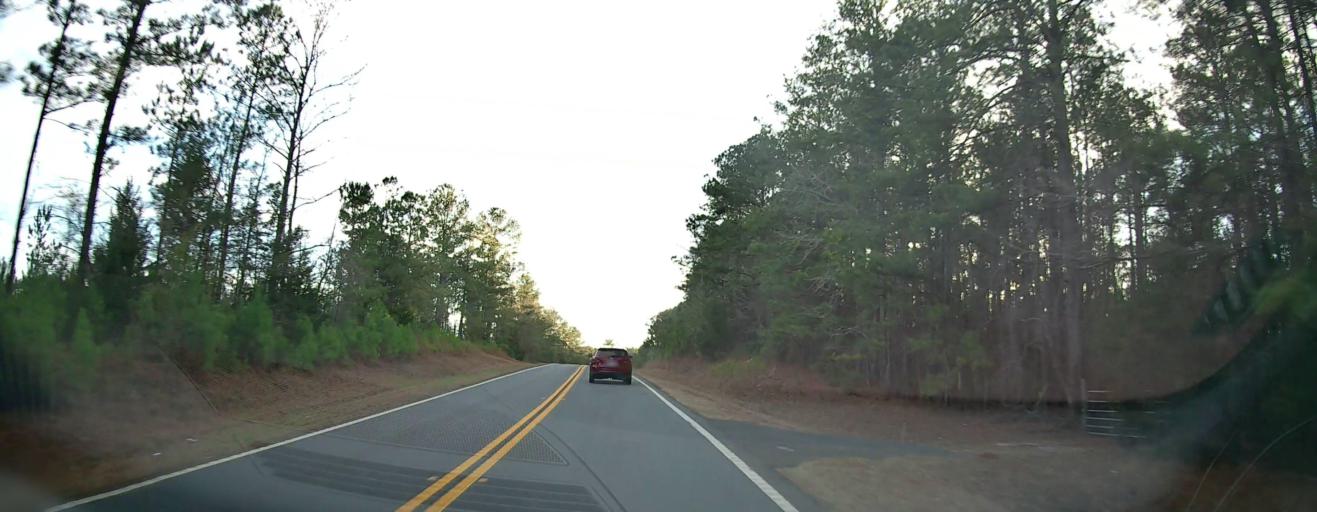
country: US
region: Georgia
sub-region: Talbot County
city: Sardis
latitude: 32.7312
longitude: -84.6209
